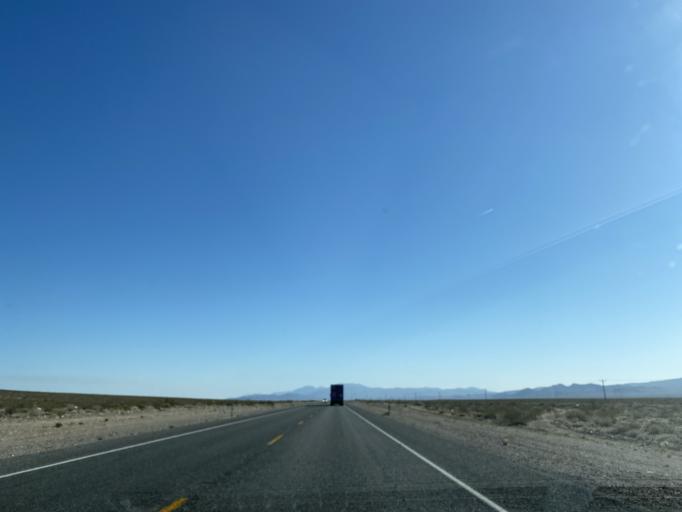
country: US
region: Nevada
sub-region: Nye County
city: Beatty
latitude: 36.8510
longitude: -116.7557
